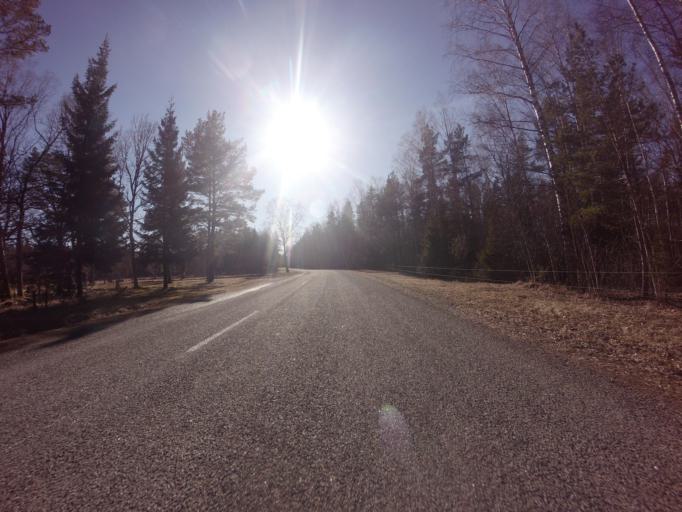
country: EE
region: Saare
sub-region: Kuressaare linn
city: Kuressaare
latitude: 58.4838
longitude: 22.2658
